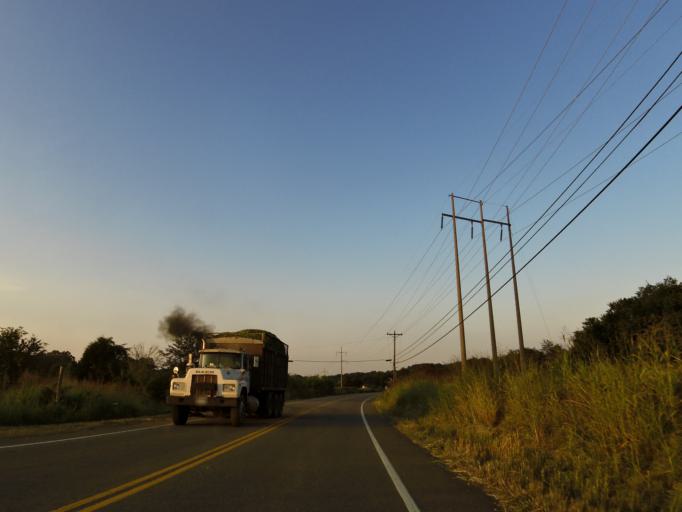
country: US
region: Tennessee
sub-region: Loudon County
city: Loudon
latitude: 35.6919
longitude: -84.3859
